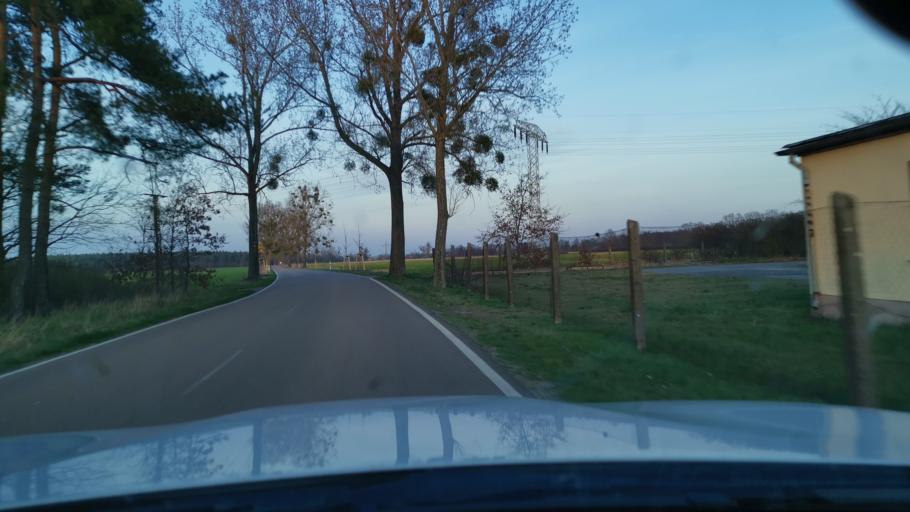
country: DE
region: Saxony-Anhalt
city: Muhlanger
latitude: 51.8571
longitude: 12.7566
